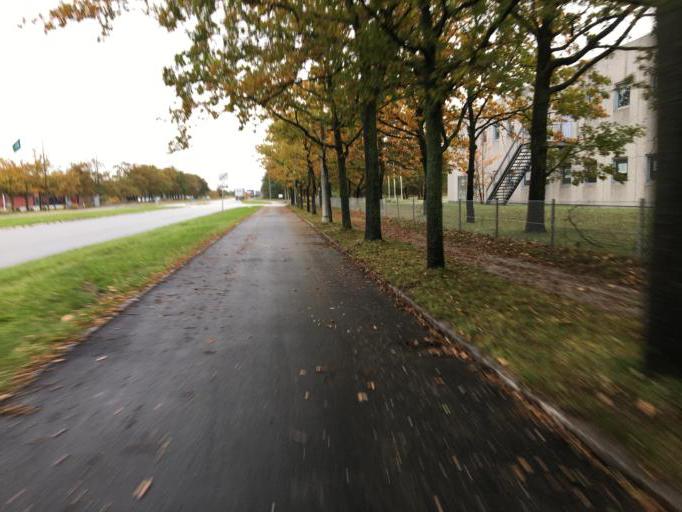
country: DK
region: Capital Region
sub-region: Hvidovre Kommune
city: Hvidovre
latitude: 55.6131
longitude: 12.4889
